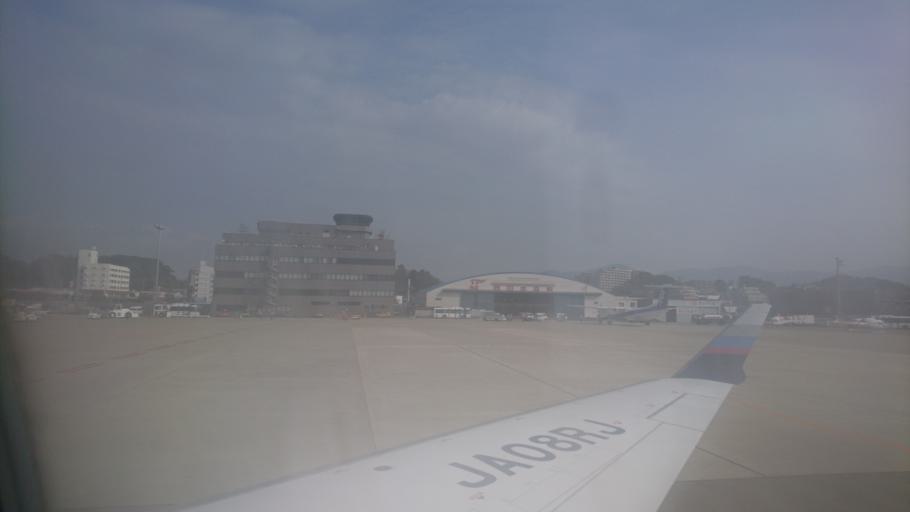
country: JP
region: Fukuoka
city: Fukuoka-shi
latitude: 33.5930
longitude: 130.4483
